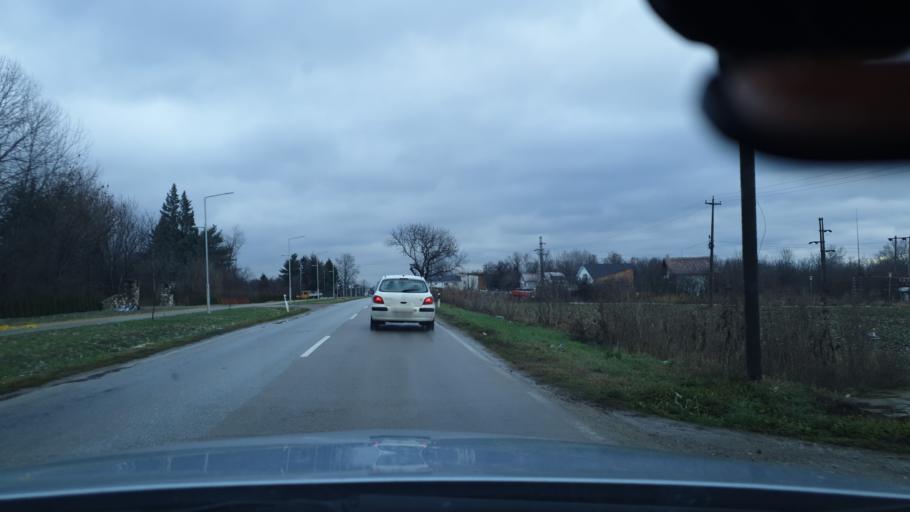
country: RS
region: Central Serbia
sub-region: Branicevski Okrug
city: Petrovac
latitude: 44.3965
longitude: 21.4039
